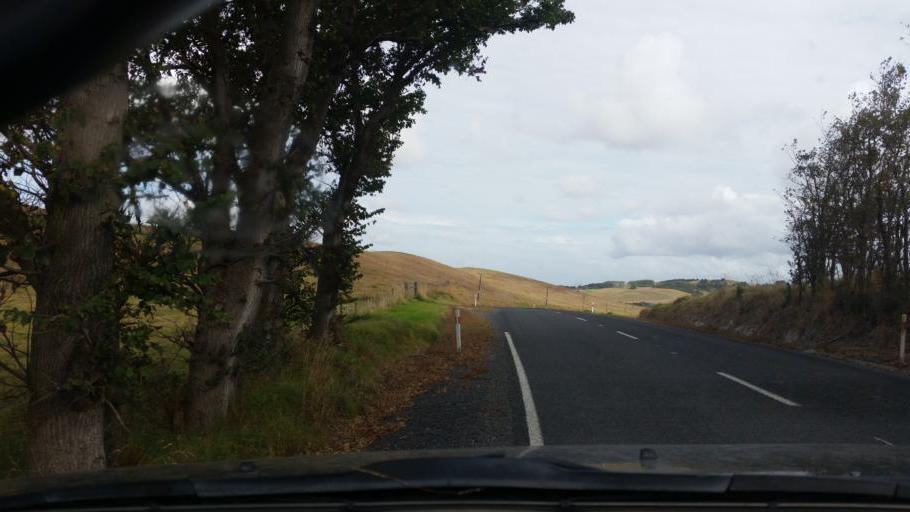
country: NZ
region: Northland
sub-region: Kaipara District
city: Dargaville
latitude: -35.9741
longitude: 173.9488
